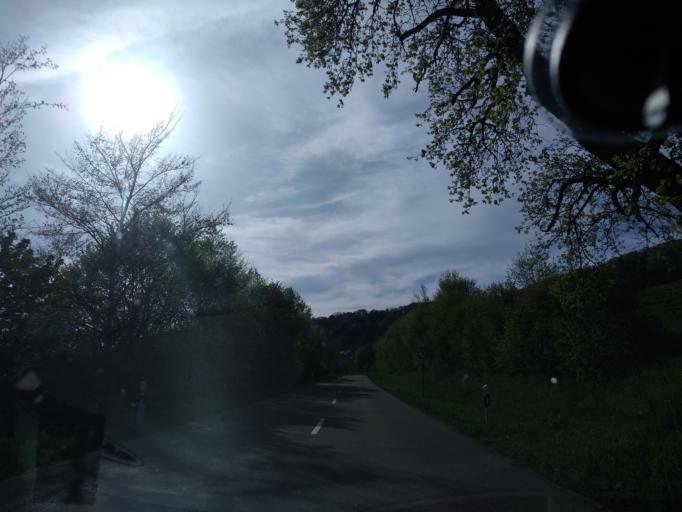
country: DE
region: Baden-Wuerttemberg
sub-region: Regierungsbezirk Stuttgart
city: Untermunkheim
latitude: 49.1611
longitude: 9.7649
